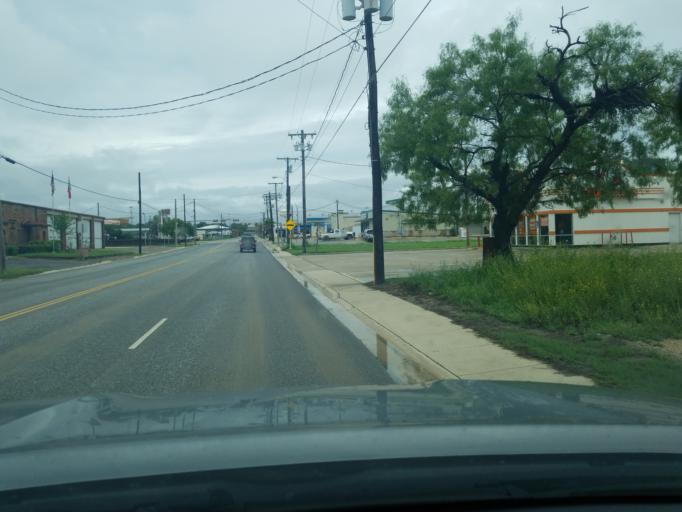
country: US
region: Texas
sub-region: Dimmit County
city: Carrizo Springs
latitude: 28.5224
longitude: -99.8549
